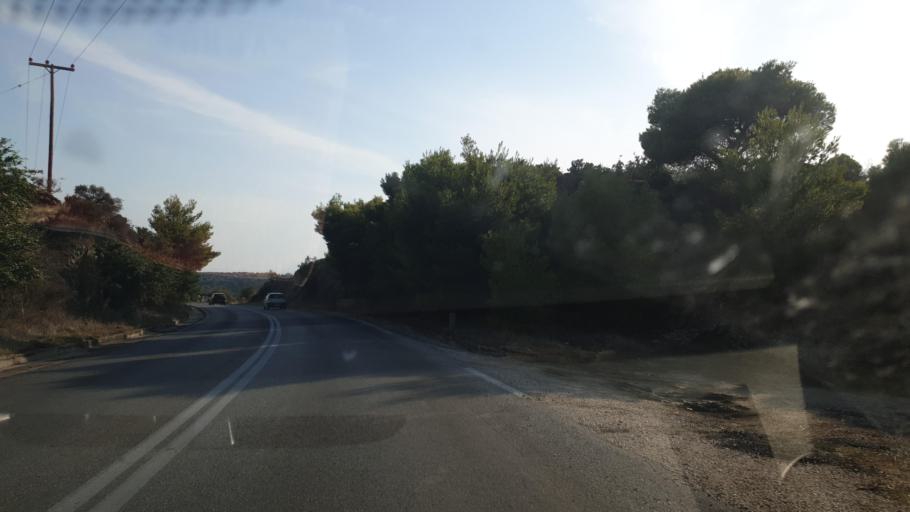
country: GR
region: Central Macedonia
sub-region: Nomos Chalkidikis
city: Nikiti
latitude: 40.2190
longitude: 23.6978
